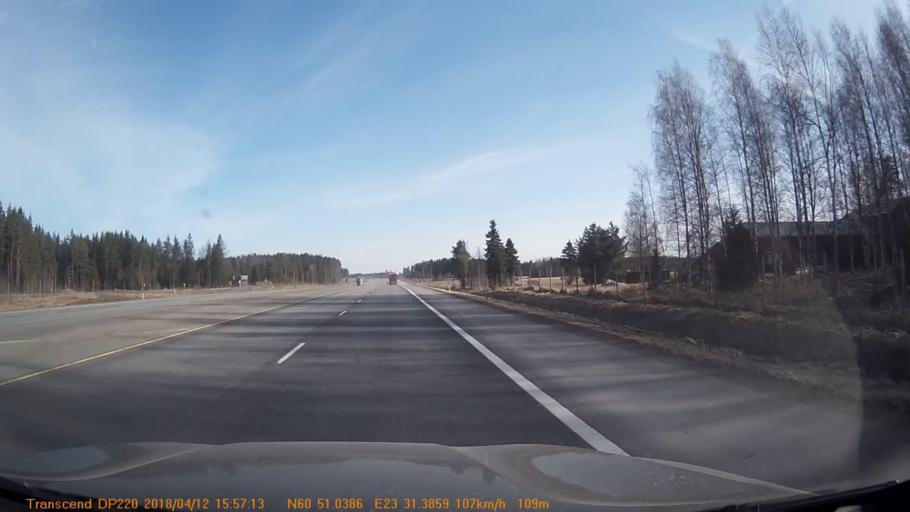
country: FI
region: Haeme
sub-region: Forssa
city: Jokioinen
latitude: 60.8506
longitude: 23.5232
